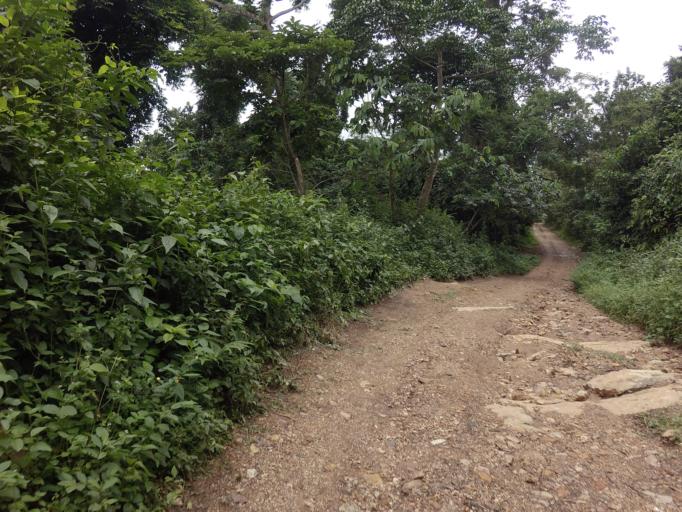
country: TG
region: Plateaux
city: Kpalime
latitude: 6.8440
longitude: 0.4422
